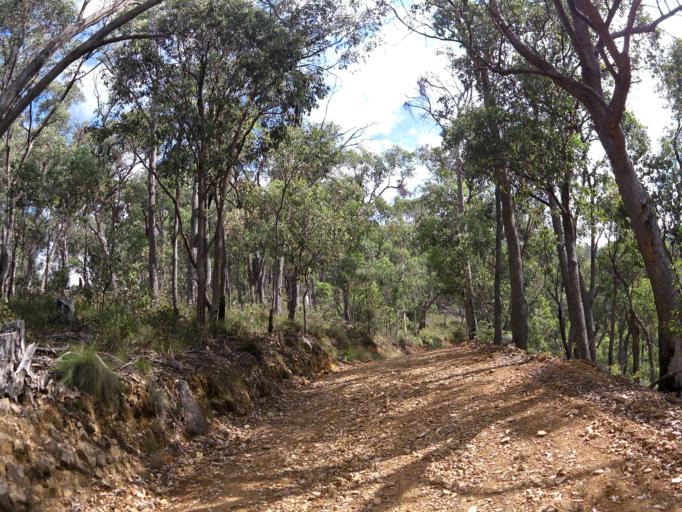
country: AU
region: Victoria
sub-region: Alpine
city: Mount Beauty
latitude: -36.7760
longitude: 147.0151
